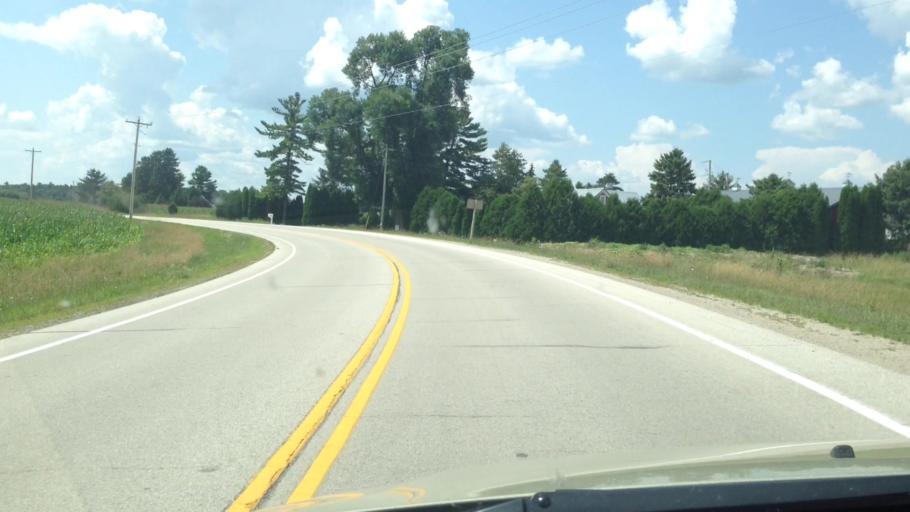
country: US
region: Wisconsin
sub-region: Brown County
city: Pulaski
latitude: 44.6588
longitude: -88.1825
